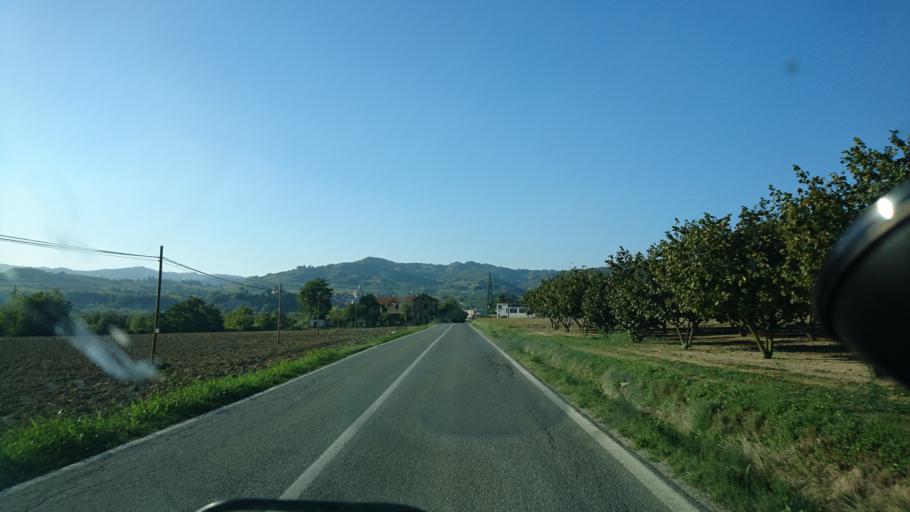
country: IT
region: Piedmont
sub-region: Provincia di Asti
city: Bubbio
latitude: 44.6569
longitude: 8.3098
